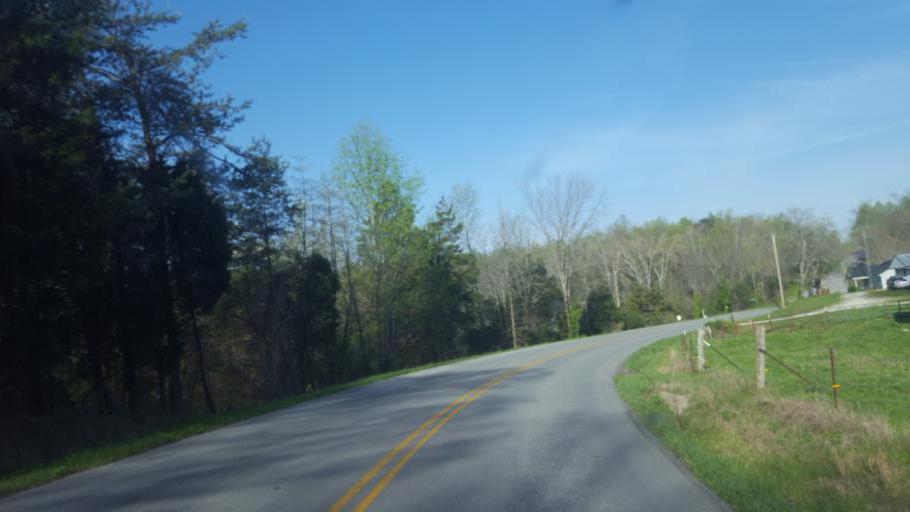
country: US
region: Kentucky
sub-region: Hart County
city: Munfordville
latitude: 37.3166
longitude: -86.0868
